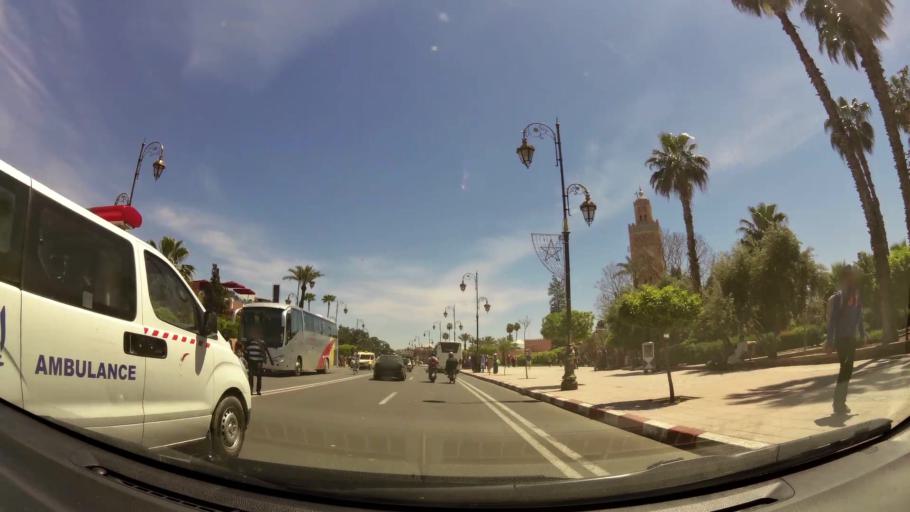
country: MA
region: Marrakech-Tensift-Al Haouz
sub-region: Marrakech
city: Marrakesh
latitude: 31.6255
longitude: -7.9942
